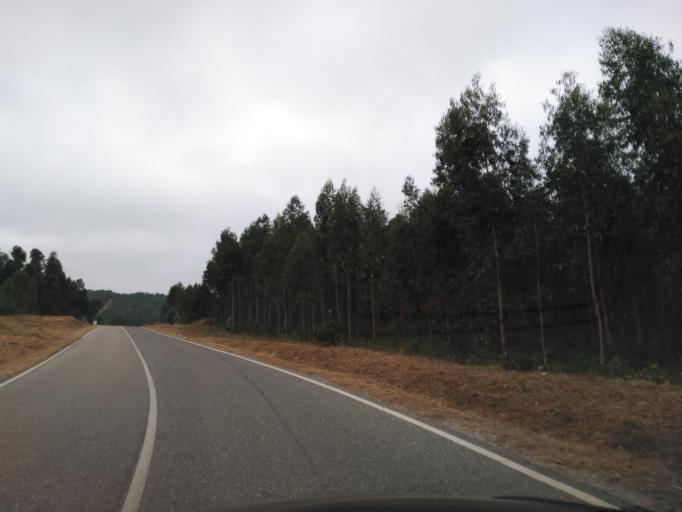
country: PT
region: Santarem
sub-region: Abrantes
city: Alferrarede
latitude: 39.5690
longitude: -8.1277
